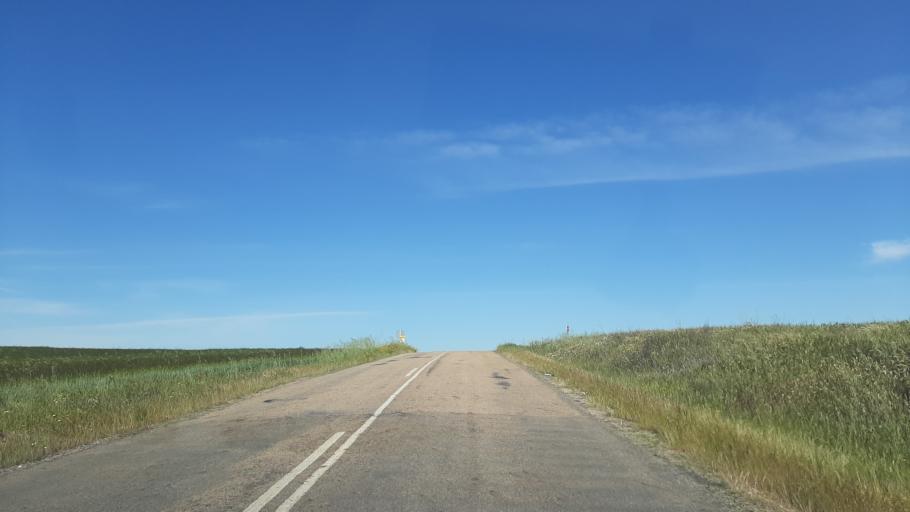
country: ES
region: Castille and Leon
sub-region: Provincia de Salamanca
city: Aldeaseca de Alba
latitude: 40.8247
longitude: -5.4261
